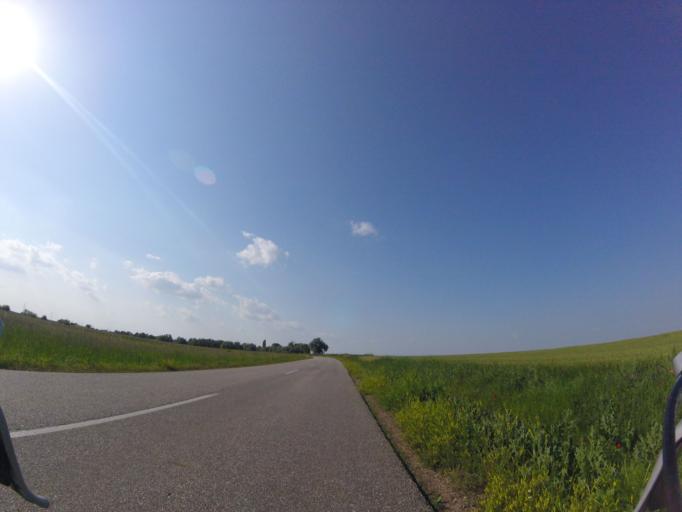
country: HU
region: Heves
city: Kiskore
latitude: 47.5458
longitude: 20.4488
